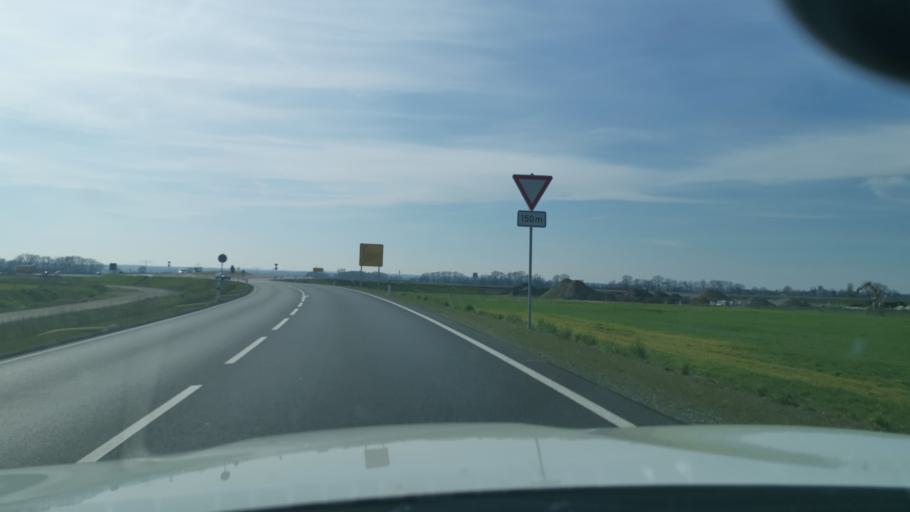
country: DE
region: Saxony-Anhalt
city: Kemberg
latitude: 51.8151
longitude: 12.6435
